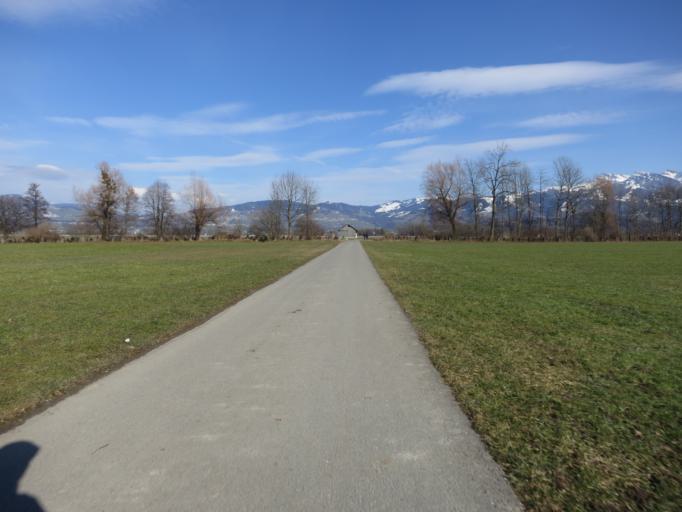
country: CH
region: Schwyz
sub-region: Bezirk March
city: Schubelbach
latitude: 47.1811
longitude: 8.9491
